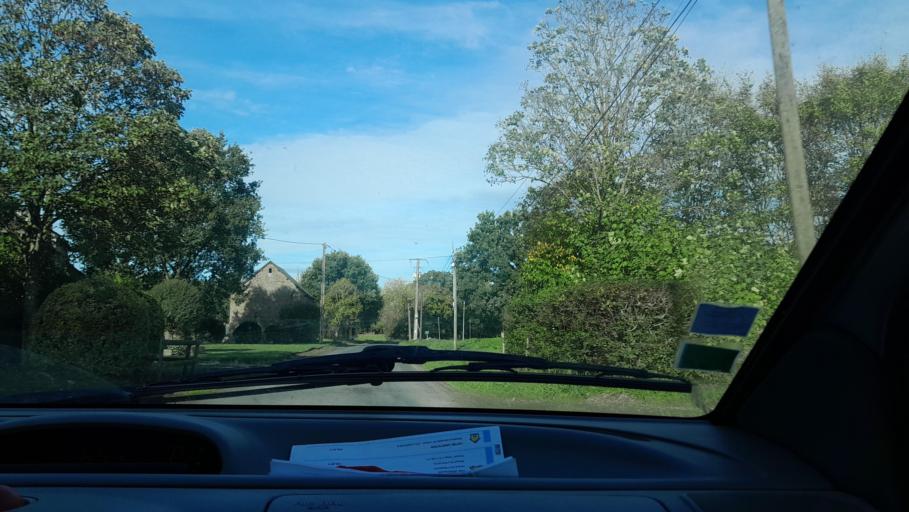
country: FR
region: Lower Normandy
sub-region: Departement de la Manche
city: Pontorson
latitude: 48.5584
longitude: -1.4600
